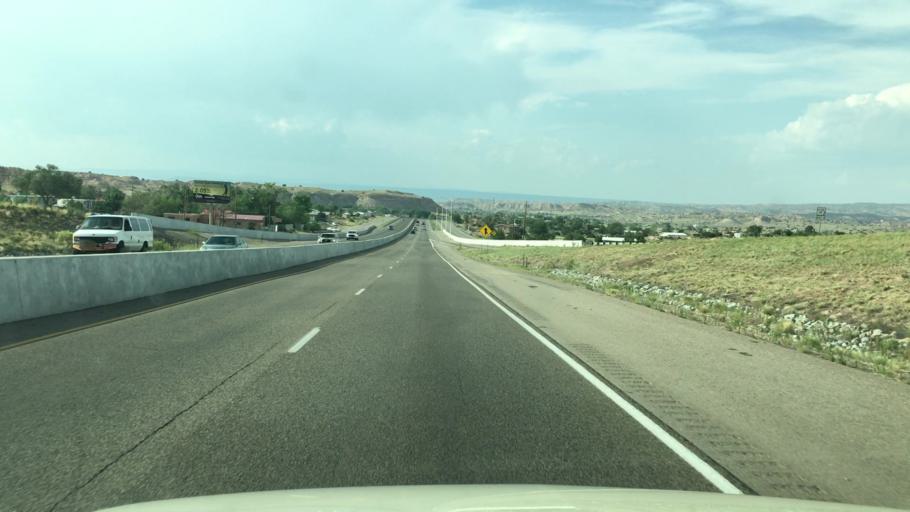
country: US
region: New Mexico
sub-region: Santa Fe County
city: El Valle de Arroyo Seco
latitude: 35.9300
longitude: -106.0178
